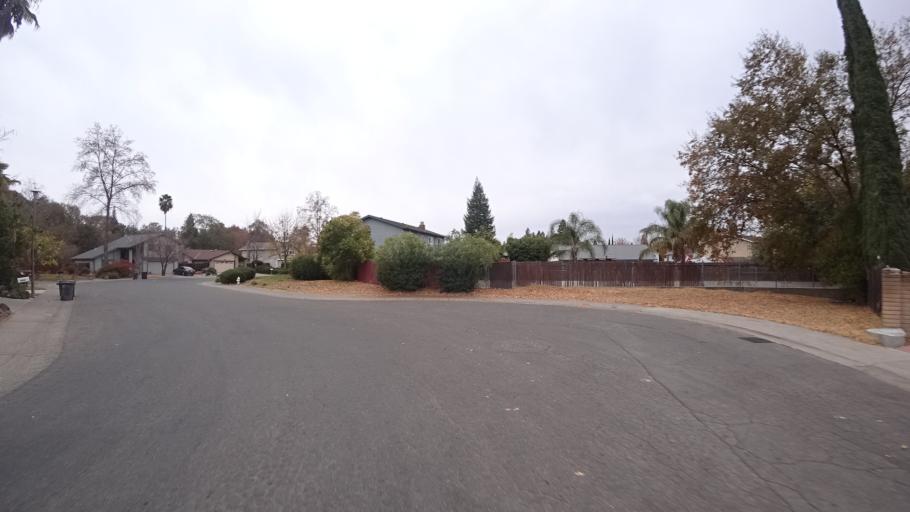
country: US
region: California
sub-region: Sacramento County
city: Citrus Heights
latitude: 38.7019
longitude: -121.3047
